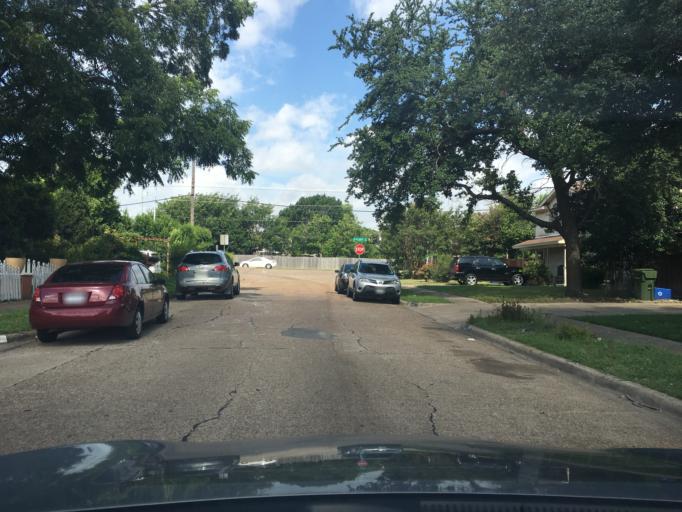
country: US
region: Texas
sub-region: Dallas County
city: Richardson
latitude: 32.9186
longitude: -96.6996
